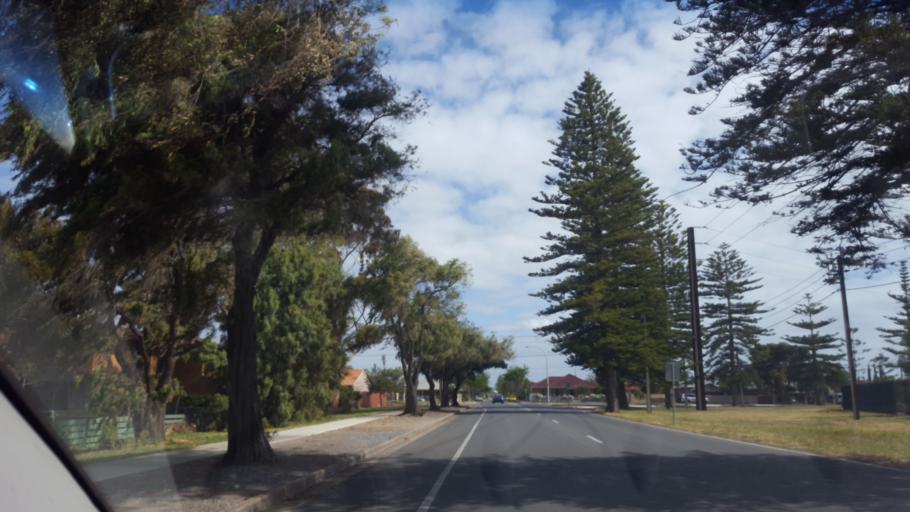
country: AU
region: South Australia
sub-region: Port Adelaide Enfield
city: Birkenhead
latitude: -34.8110
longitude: 138.4966
